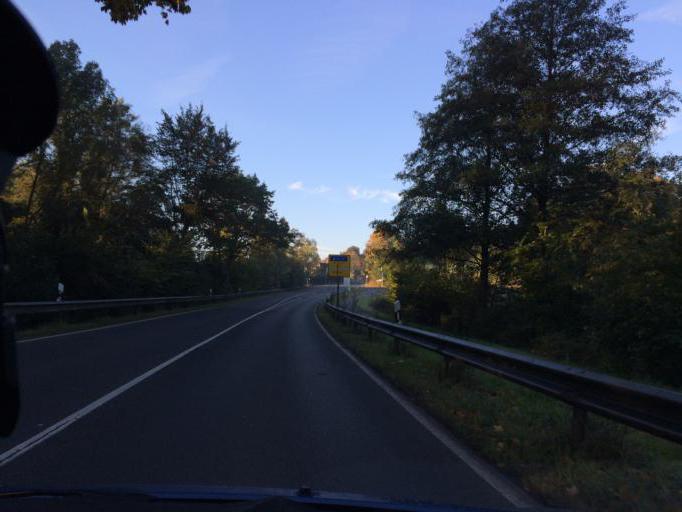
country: DE
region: North Rhine-Westphalia
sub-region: Regierungsbezirk Koln
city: Wachtberg
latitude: 50.6435
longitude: 7.0979
